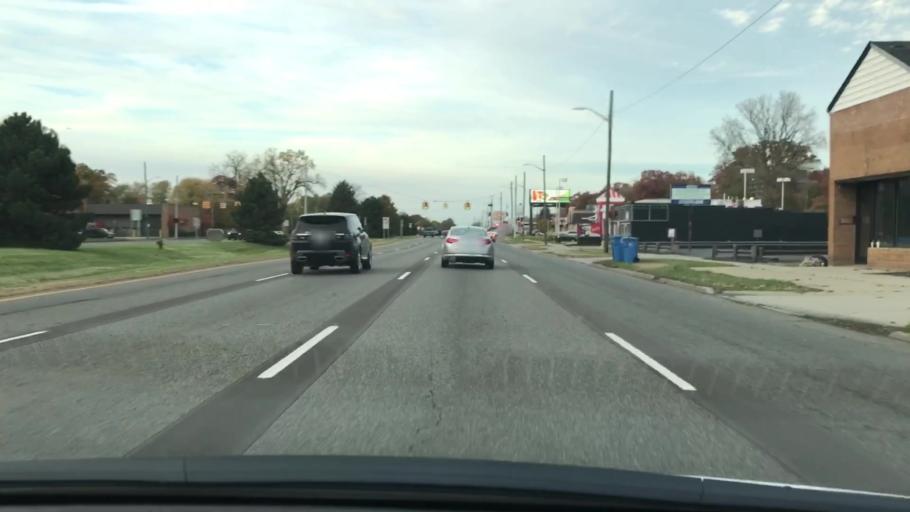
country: US
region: Michigan
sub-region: Wayne County
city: Taylor
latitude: 42.2751
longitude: -83.2703
